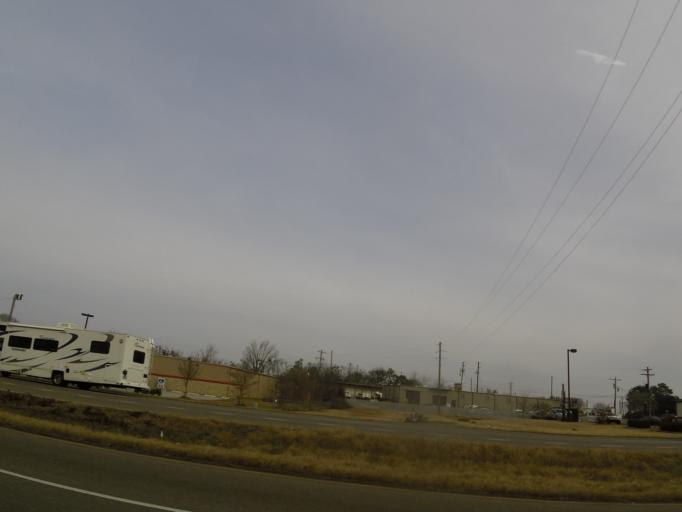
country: US
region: Alabama
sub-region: Montgomery County
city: Montgomery
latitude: 32.3124
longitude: -86.2239
